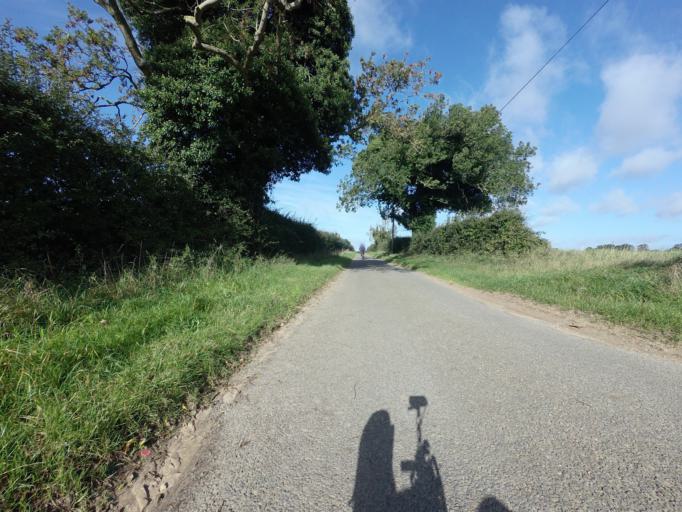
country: GB
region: England
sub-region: Norfolk
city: Dersingham
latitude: 52.8526
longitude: 0.6672
